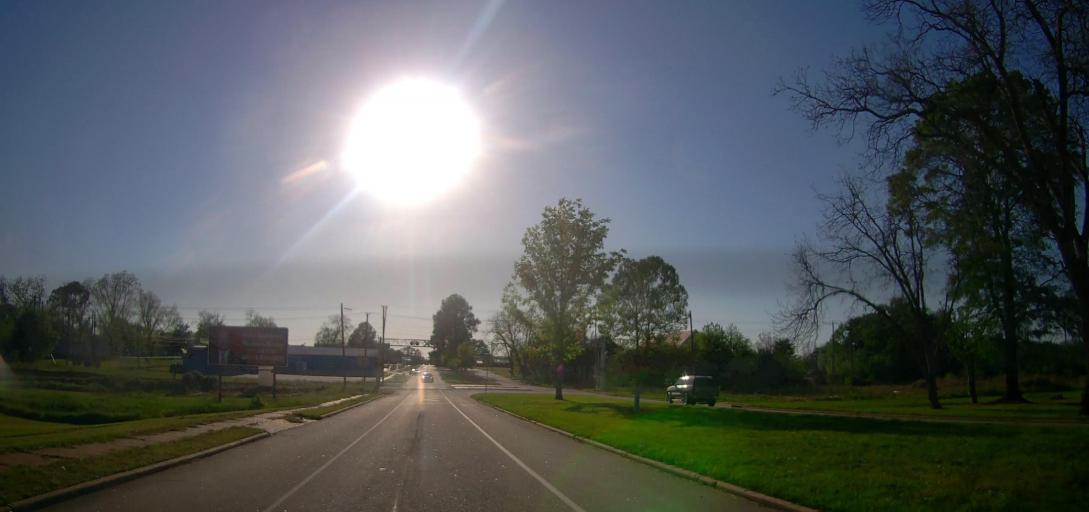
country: US
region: Georgia
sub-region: Ben Hill County
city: Fitzgerald
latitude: 31.7148
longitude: -83.2455
